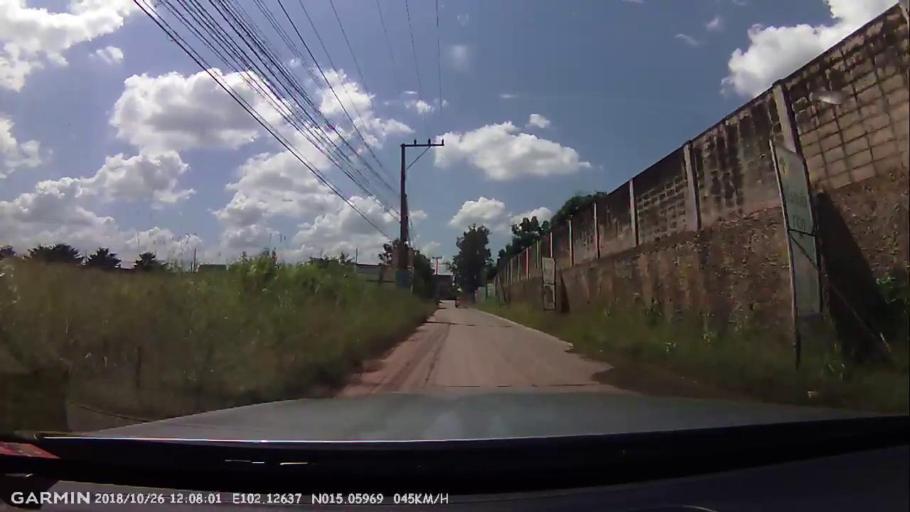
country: TH
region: Nakhon Ratchasima
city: Nakhon Ratchasima
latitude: 15.0596
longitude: 102.1263
